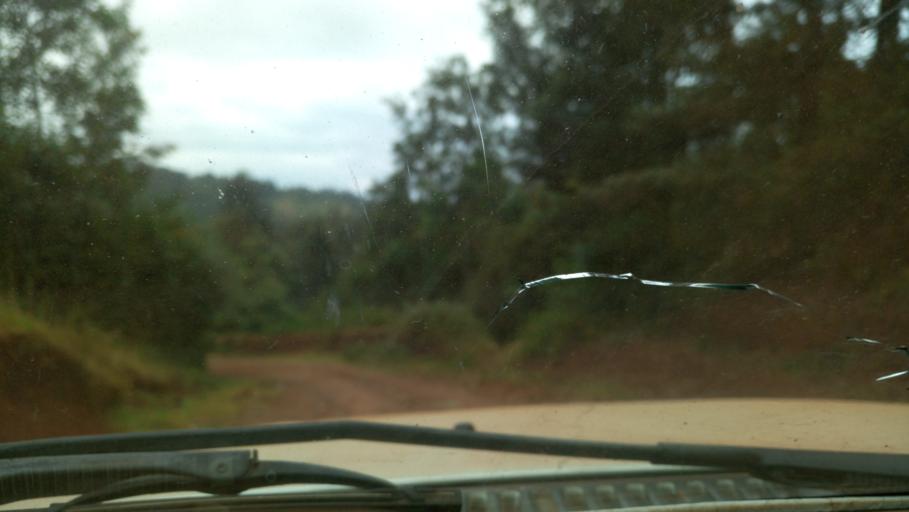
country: KE
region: Murang'a District
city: Maragua
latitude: -0.7601
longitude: 37.0377
